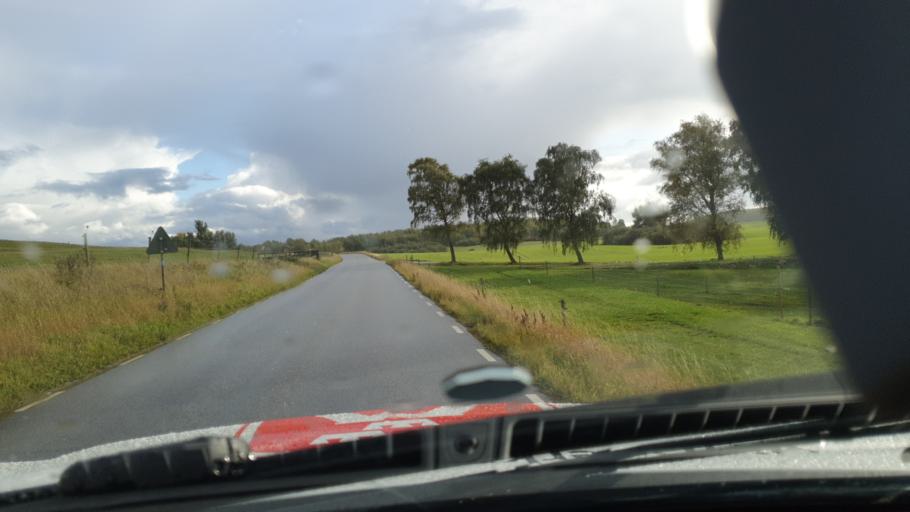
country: SE
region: Skane
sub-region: Malmo
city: Oxie
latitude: 55.5281
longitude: 13.1006
